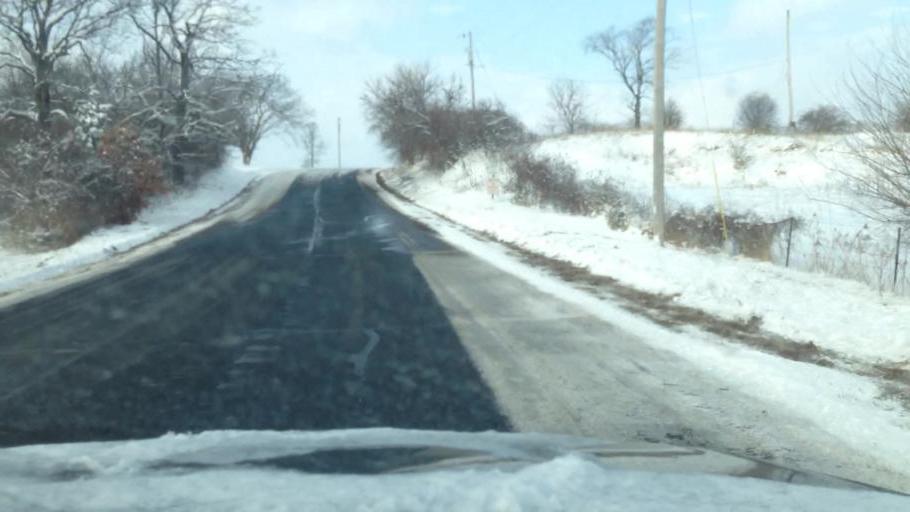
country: US
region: Wisconsin
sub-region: Walworth County
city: East Troy
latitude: 42.7554
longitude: -88.4455
